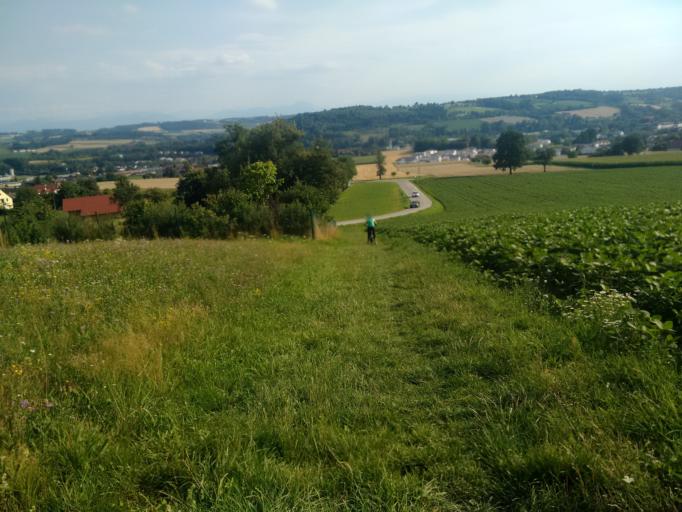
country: AT
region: Upper Austria
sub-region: Politischer Bezirk Grieskirchen
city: Bad Schallerbach
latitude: 48.2393
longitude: 13.9305
